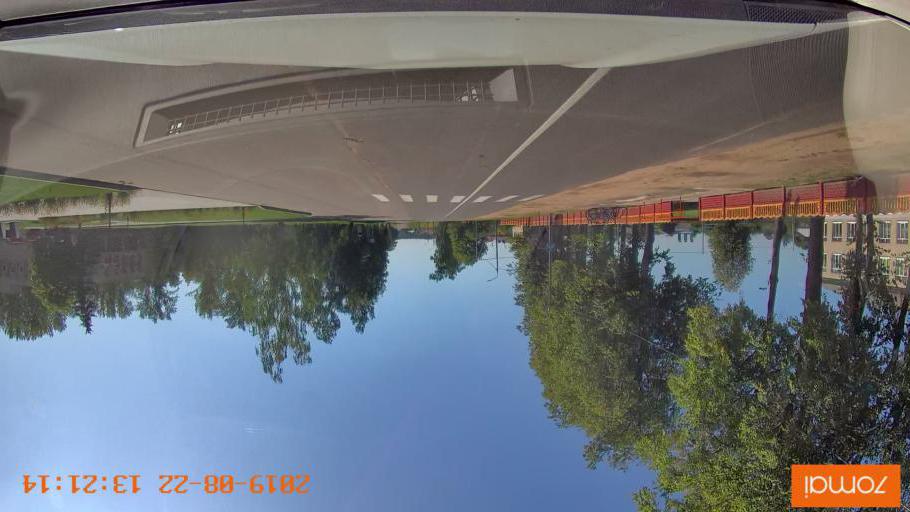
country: BY
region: Minsk
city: Urechcha
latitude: 53.2256
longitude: 27.9784
